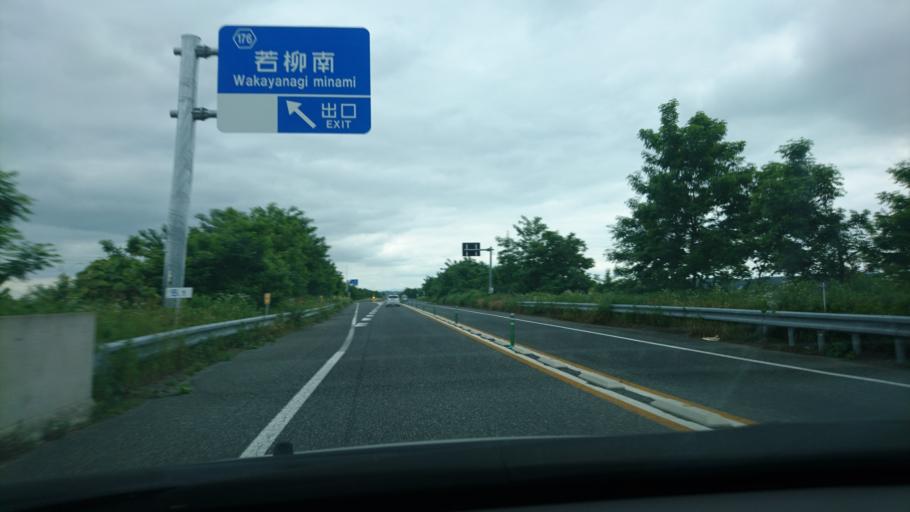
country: JP
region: Iwate
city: Ichinoseki
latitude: 38.7360
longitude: 141.1249
